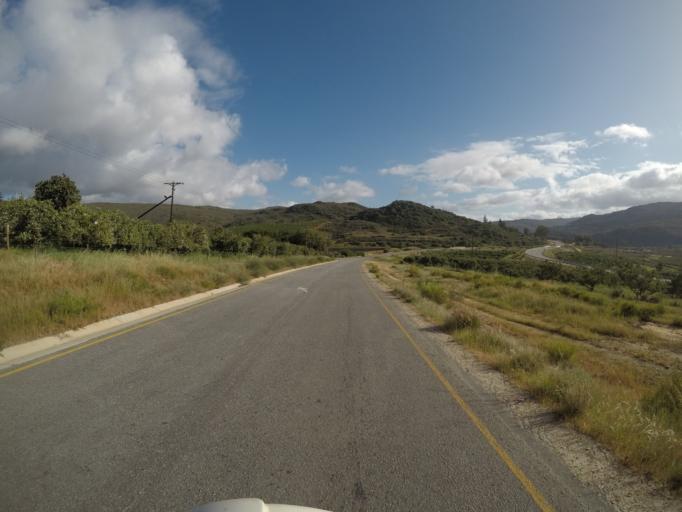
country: ZA
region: Western Cape
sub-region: West Coast District Municipality
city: Clanwilliam
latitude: -32.4333
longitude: 18.9541
